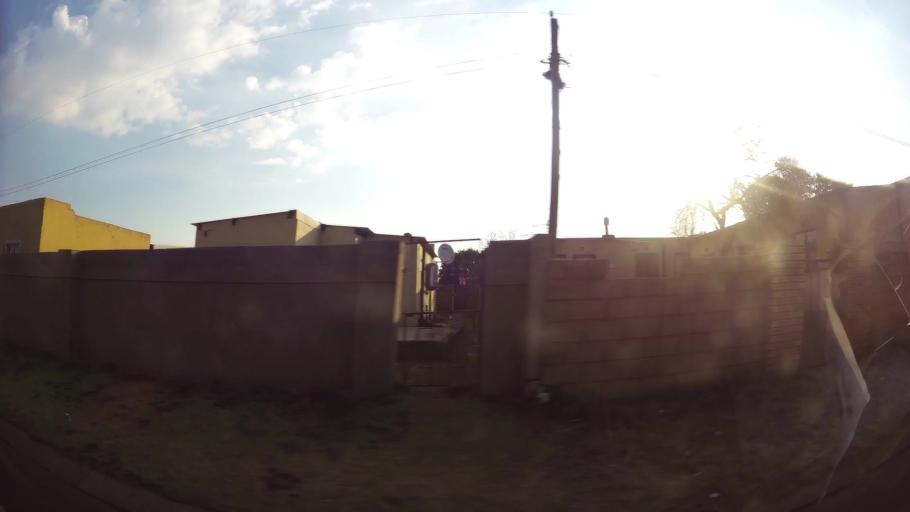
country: ZA
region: Gauteng
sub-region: Ekurhuleni Metropolitan Municipality
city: Germiston
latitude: -26.3589
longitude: 28.2280
